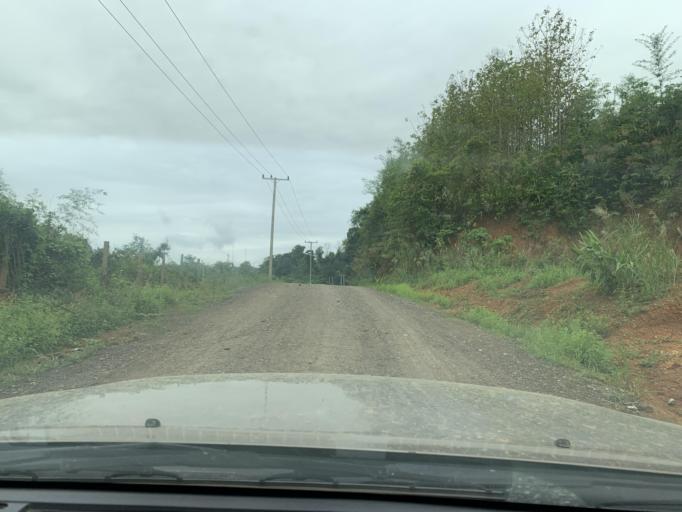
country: TH
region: Nan
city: Mae Charim
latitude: 18.4179
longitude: 101.4604
